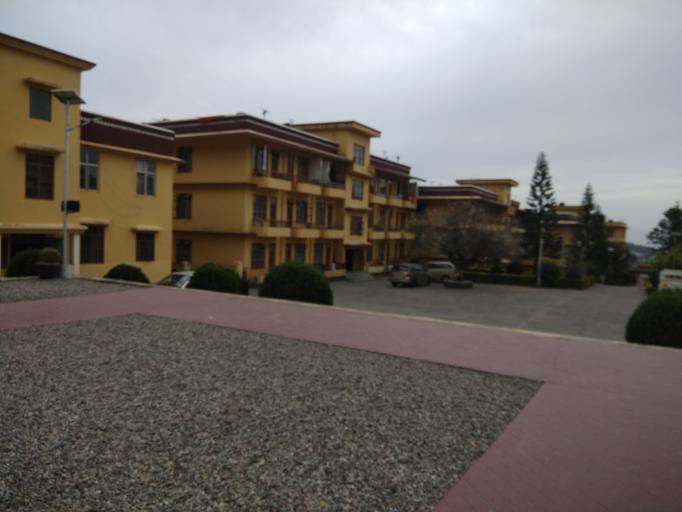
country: IN
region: Himachal Pradesh
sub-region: Kangra
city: Dharmsala
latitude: 32.1870
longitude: 76.3685
